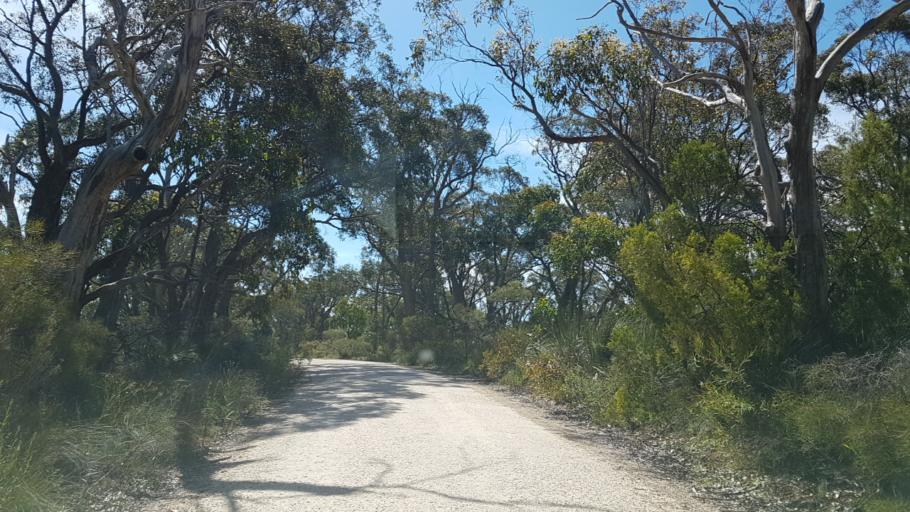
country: AU
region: South Australia
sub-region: Adelaide Hills
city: Adelaide Hills
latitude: -34.9019
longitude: 138.7283
